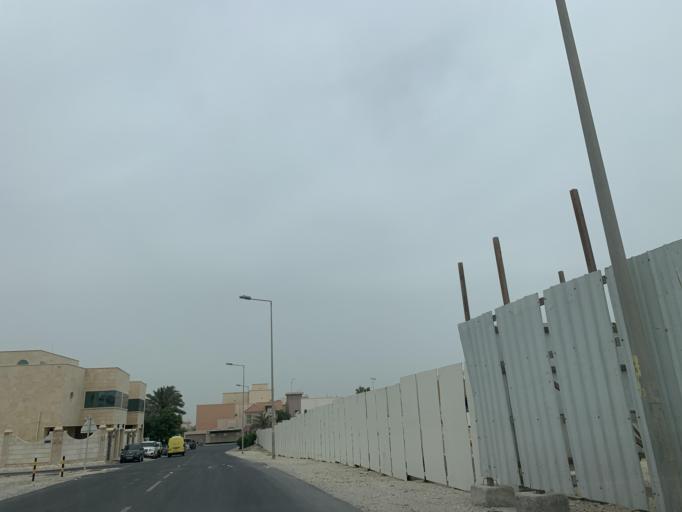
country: BH
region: Northern
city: Ar Rifa'
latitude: 26.1377
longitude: 50.5559
